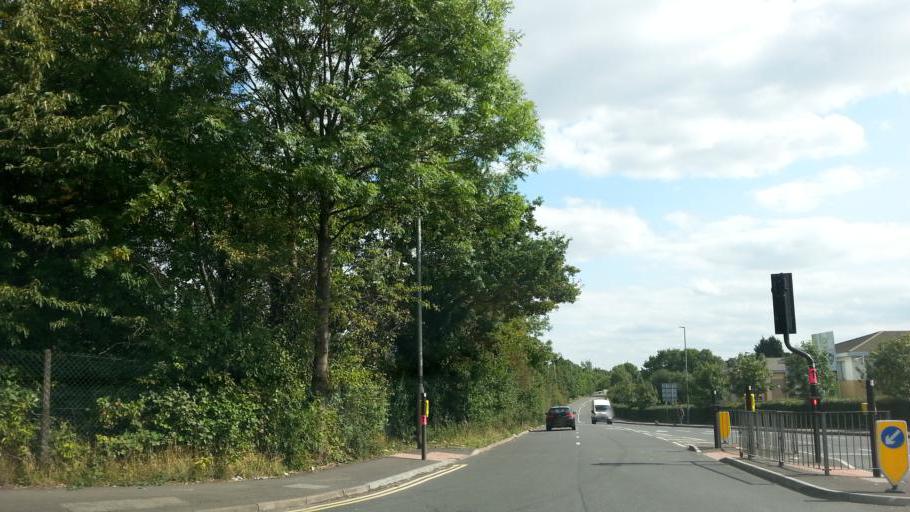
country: GB
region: England
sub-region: Leicestershire
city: Kirby Muxloe
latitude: 52.6304
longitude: -1.2085
